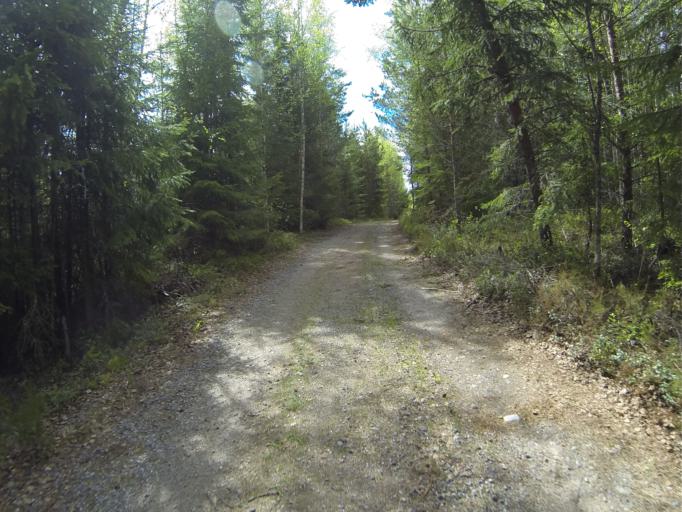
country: FI
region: Varsinais-Suomi
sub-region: Salo
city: Halikko
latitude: 60.3058
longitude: 23.0759
